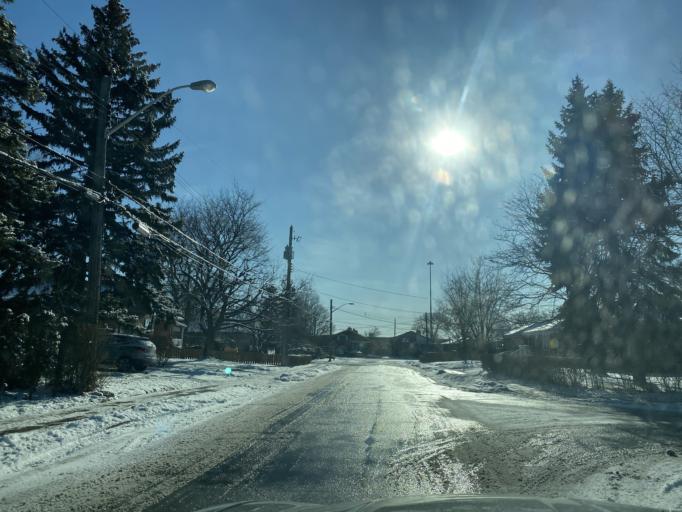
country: CA
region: Ontario
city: Scarborough
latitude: 43.7707
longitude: -79.3108
